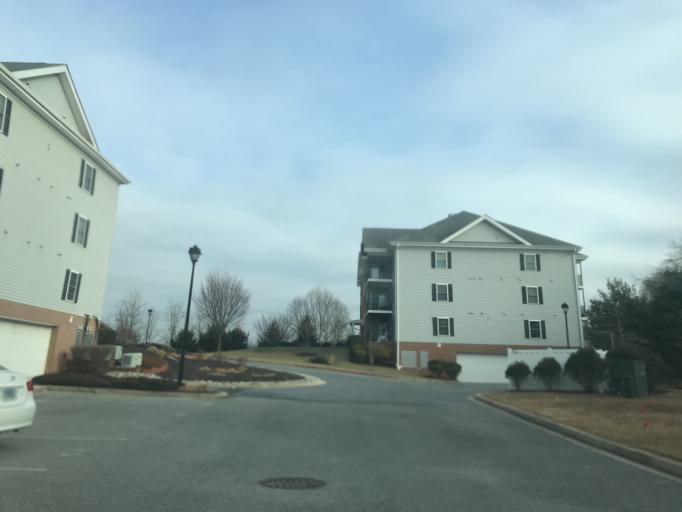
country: US
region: Maryland
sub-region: Carroll County
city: Eldersburg
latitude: 39.3929
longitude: -76.9141
